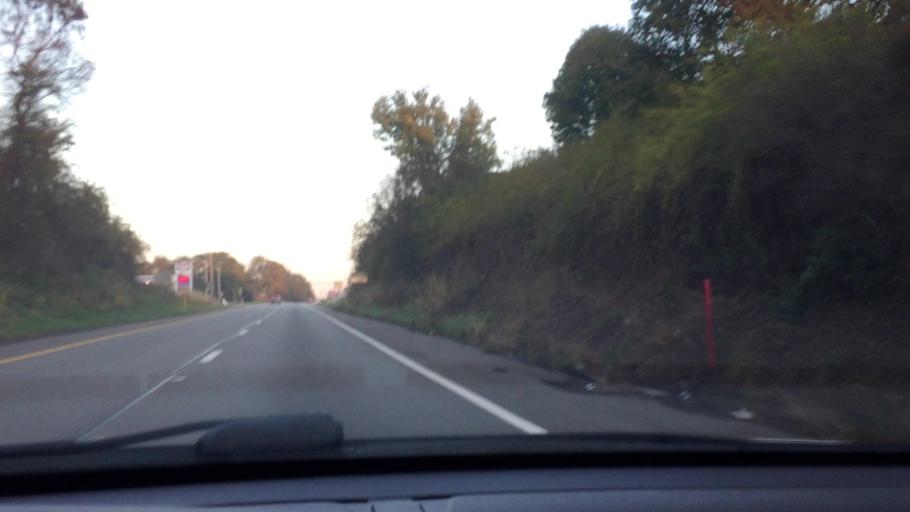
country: US
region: Pennsylvania
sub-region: Westmoreland County
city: Fellsburg
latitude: 40.1998
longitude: -79.8321
